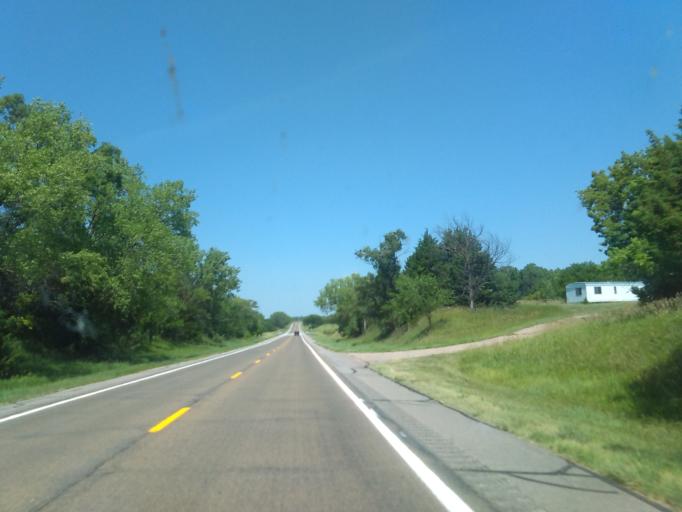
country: US
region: Nebraska
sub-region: Hayes County
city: Hayes Center
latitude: 40.7383
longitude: -100.7183
